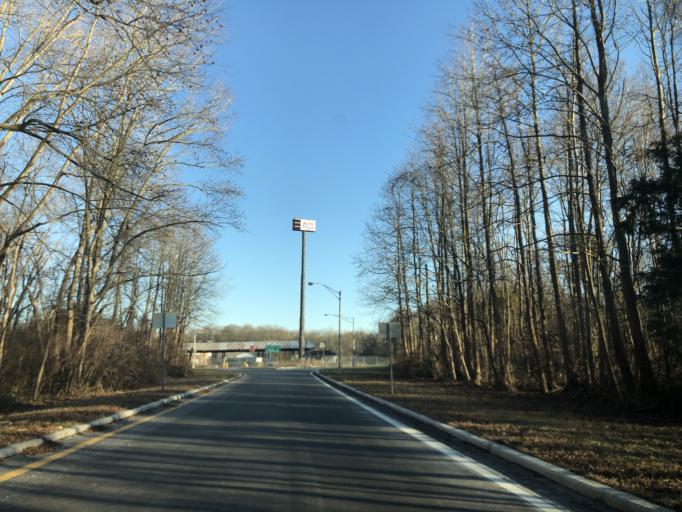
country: US
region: New Jersey
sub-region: Gloucester County
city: Beckett
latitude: 39.7304
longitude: -75.4070
